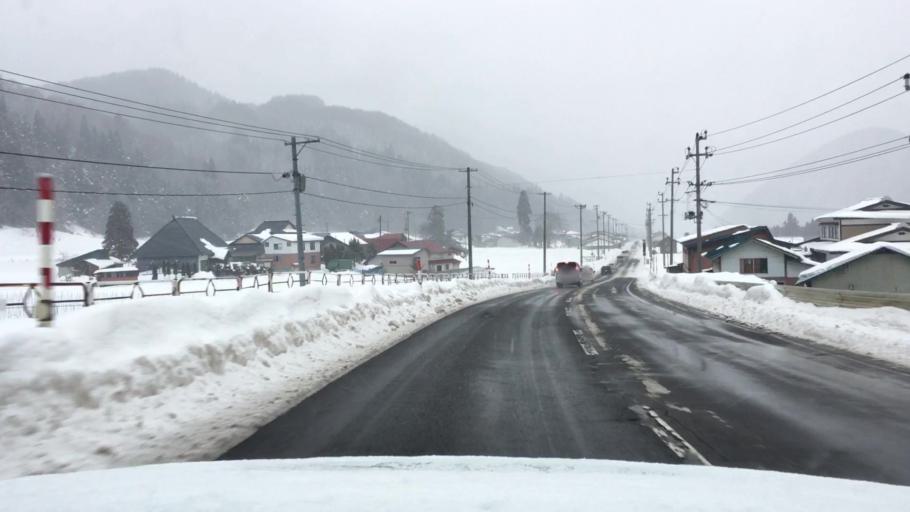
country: JP
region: Akita
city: Hanawa
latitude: 40.0654
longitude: 141.0154
